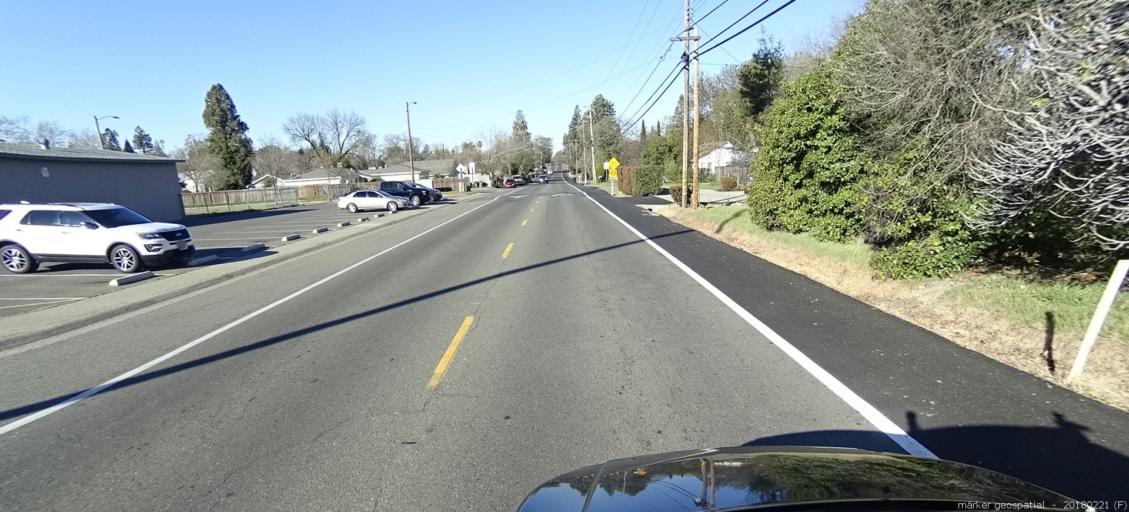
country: US
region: California
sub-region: Sacramento County
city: Orangevale
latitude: 38.6858
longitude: -121.2317
